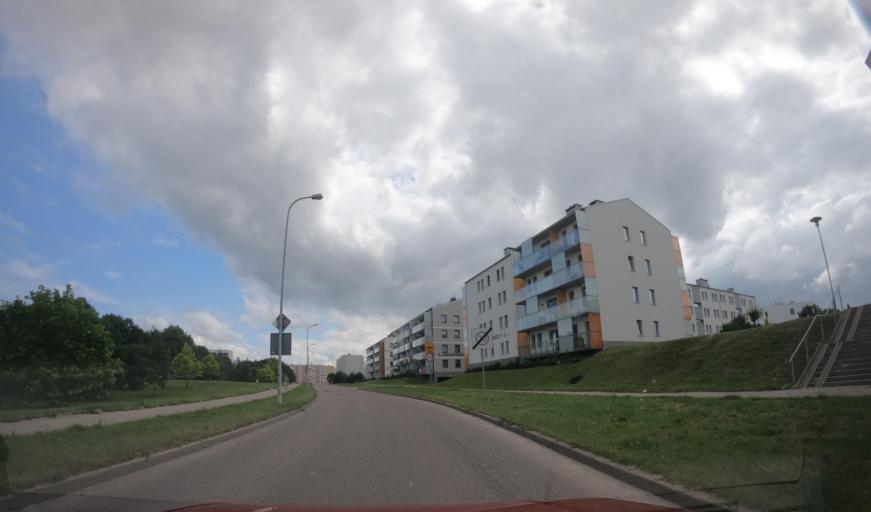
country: PL
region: West Pomeranian Voivodeship
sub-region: Koszalin
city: Koszalin
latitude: 54.2103
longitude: 16.1874
